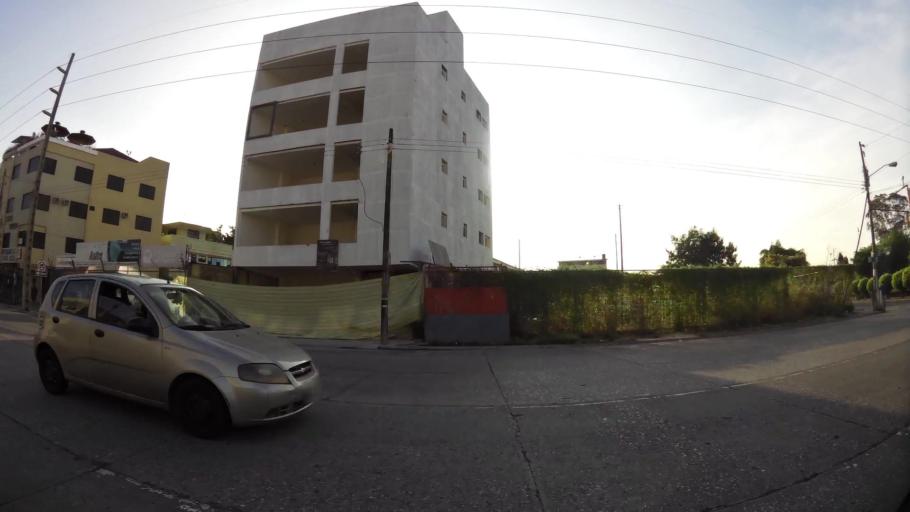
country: EC
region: Guayas
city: Eloy Alfaro
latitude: -2.1612
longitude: -79.8954
